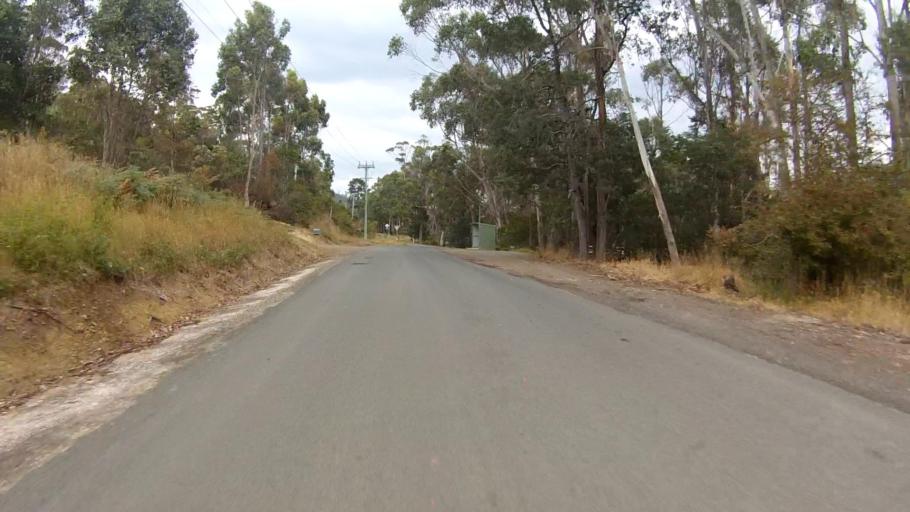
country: AU
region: Tasmania
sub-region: Huon Valley
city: Cygnet
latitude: -43.2407
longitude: 147.1520
